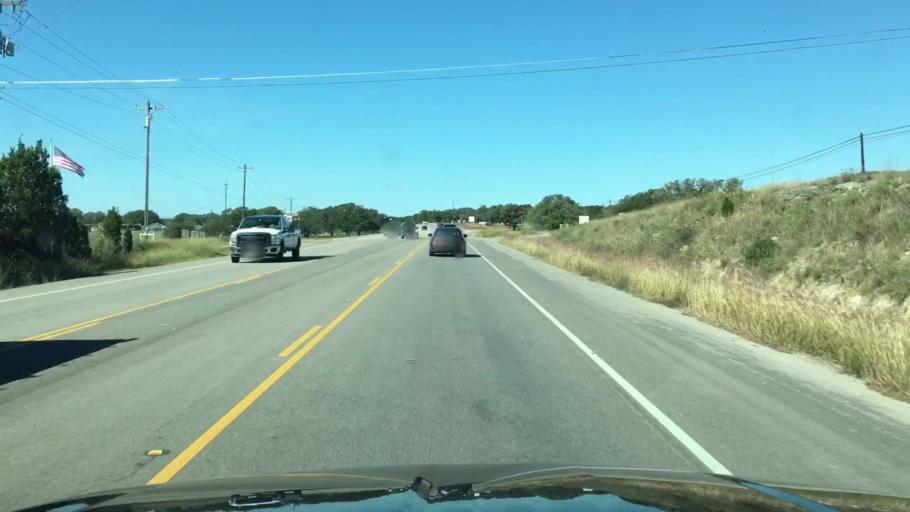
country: US
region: Texas
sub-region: Hays County
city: Dripping Springs
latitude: 30.1983
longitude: -98.1796
